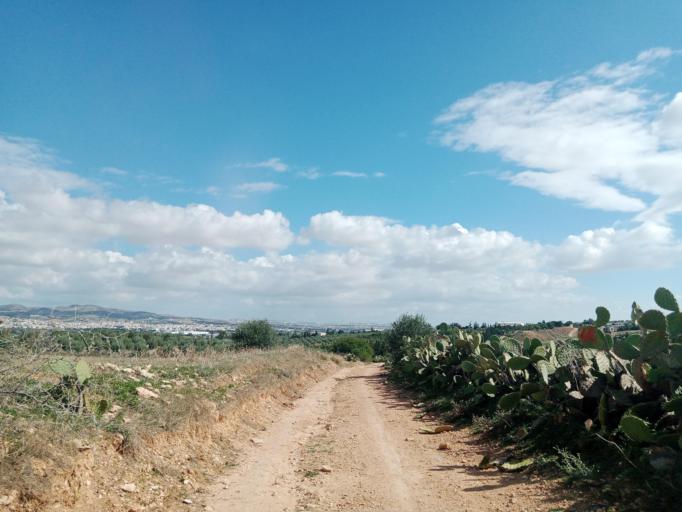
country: TN
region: Tunis
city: Oued Lill
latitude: 36.8172
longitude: 10.0026
